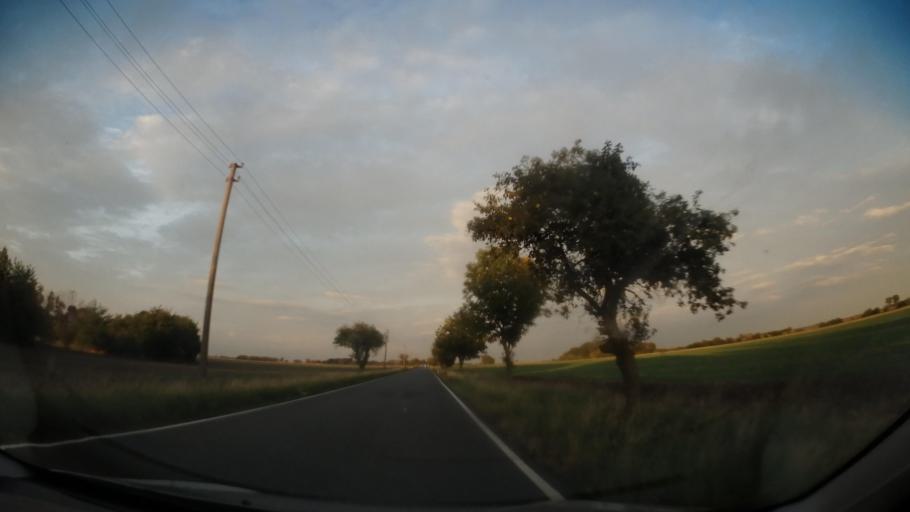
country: CZ
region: Central Bohemia
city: Loucen
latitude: 50.2360
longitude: 14.9817
